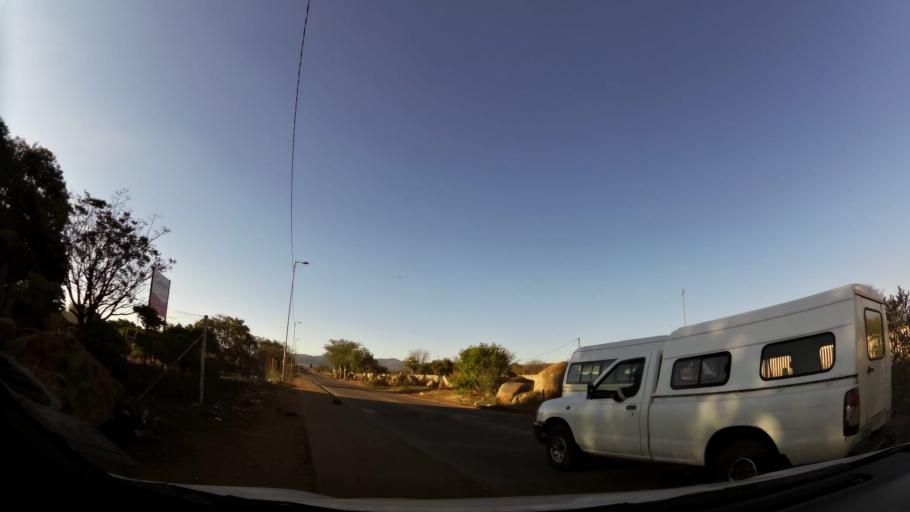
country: ZA
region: Limpopo
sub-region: Waterberg District Municipality
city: Mokopane
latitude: -24.1487
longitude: 28.9874
